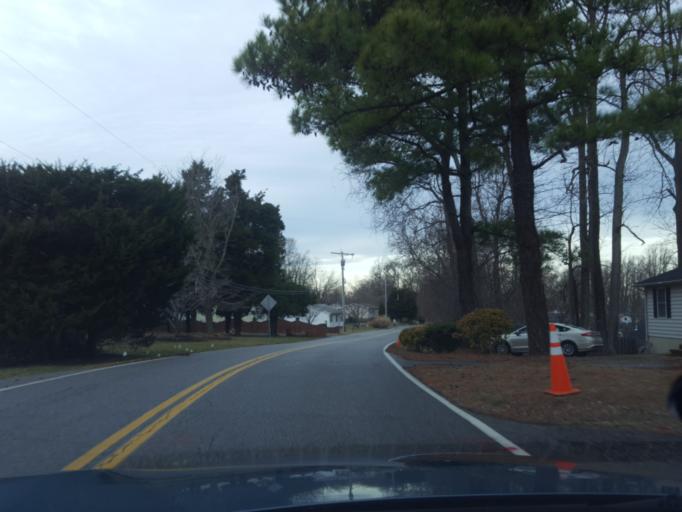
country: US
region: Maryland
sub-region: Calvert County
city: Chesapeake Beach
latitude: 38.6658
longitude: -76.5387
